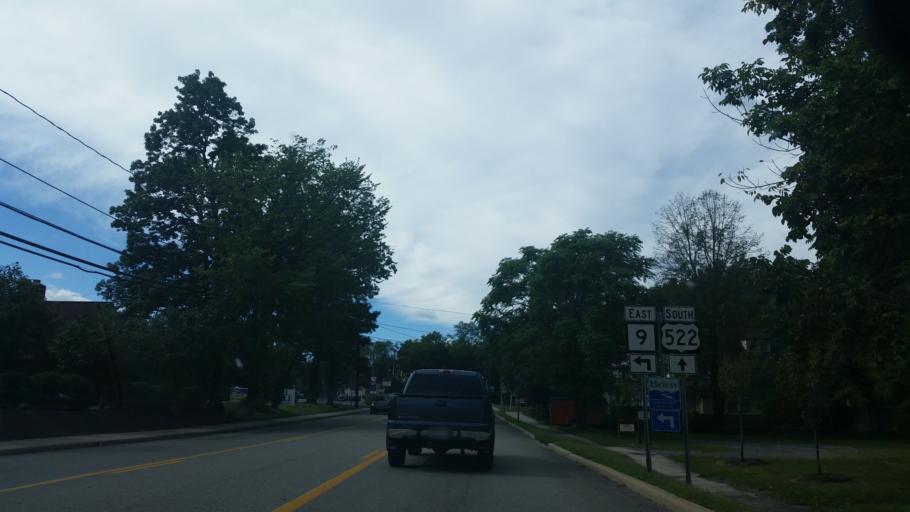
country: US
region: West Virginia
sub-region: Morgan County
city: Berkeley Springs
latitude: 39.6252
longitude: -78.2290
